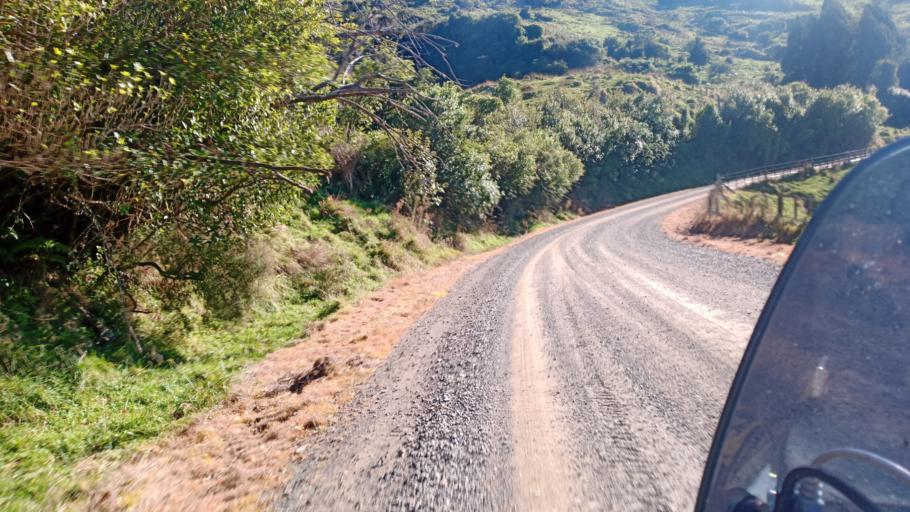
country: NZ
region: Hawke's Bay
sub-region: Wairoa District
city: Wairoa
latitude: -38.7487
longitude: 177.2690
